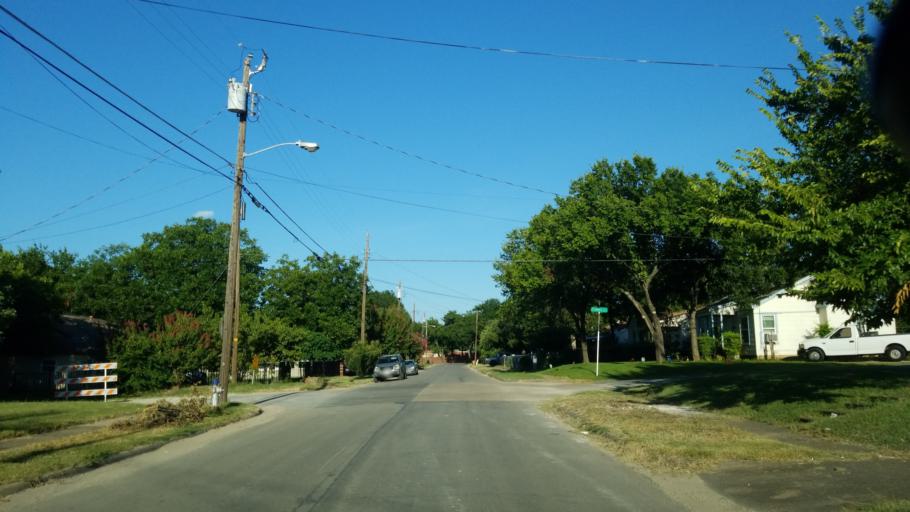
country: US
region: Texas
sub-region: Dallas County
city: Balch Springs
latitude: 32.7766
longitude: -96.7045
